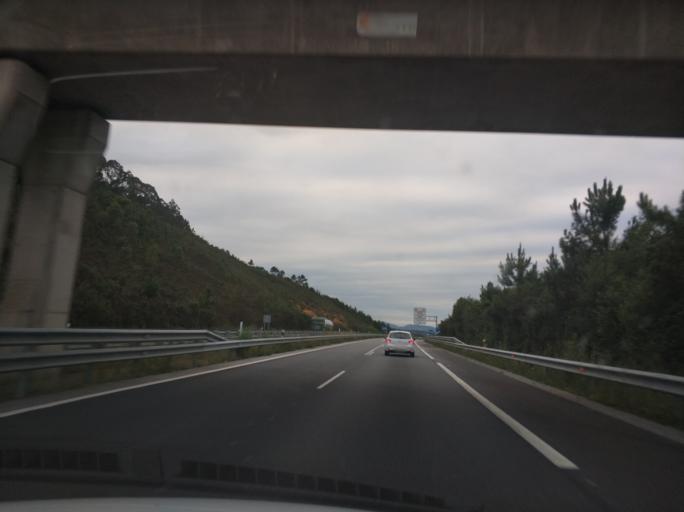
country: ES
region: Asturias
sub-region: Province of Asturias
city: Tineo
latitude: 43.5454
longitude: -6.4394
